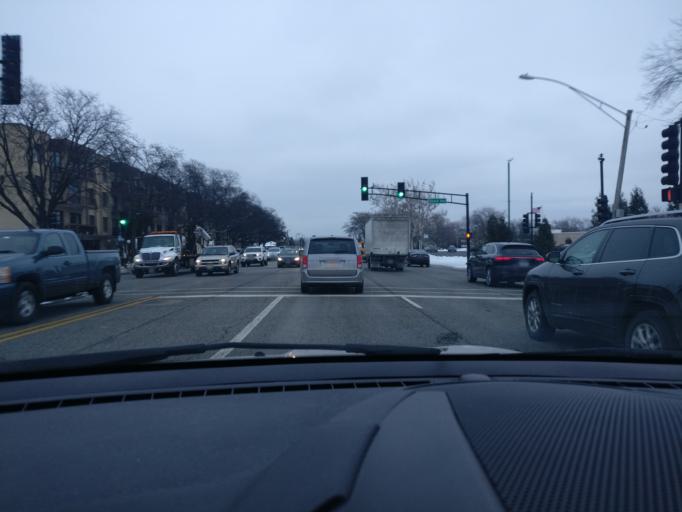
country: US
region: Illinois
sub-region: Cook County
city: Niles
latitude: 42.0404
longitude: -87.8202
